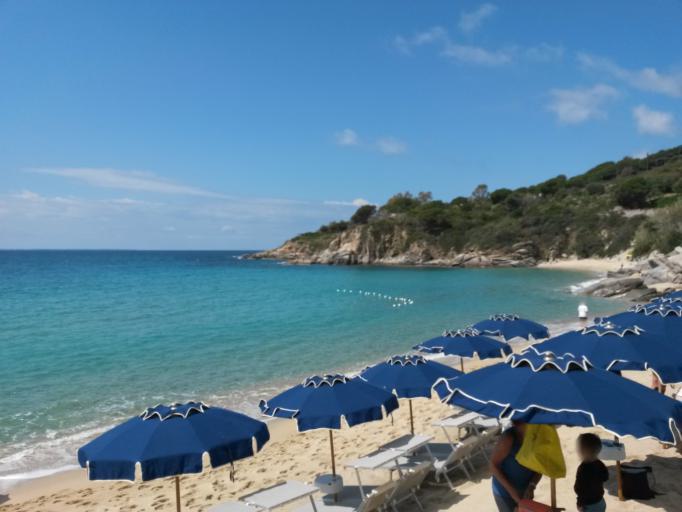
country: IT
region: Tuscany
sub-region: Provincia di Livorno
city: Campo nell'Elba
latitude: 42.7374
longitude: 10.1861
